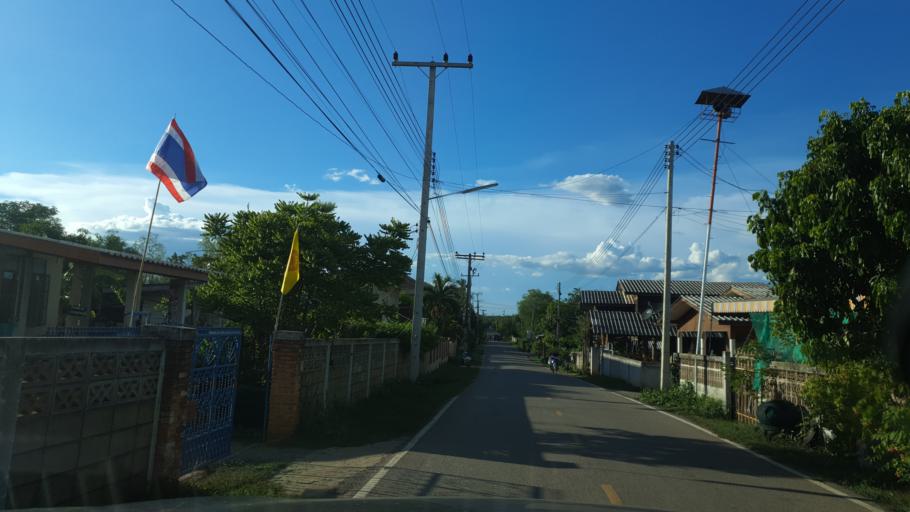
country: TH
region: Lampang
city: Sop Prap
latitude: 17.8856
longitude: 99.3115
